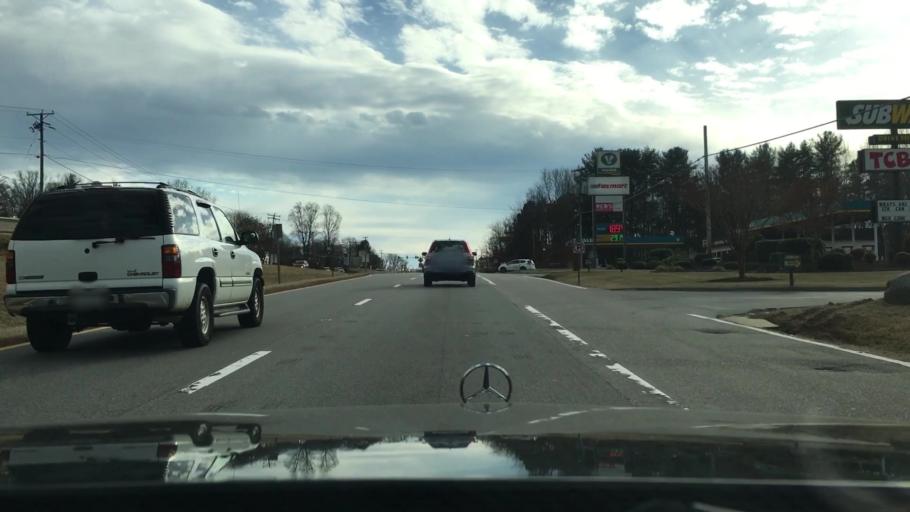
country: US
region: Virginia
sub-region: Pittsylvania County
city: Chatham
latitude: 36.7928
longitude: -79.3940
